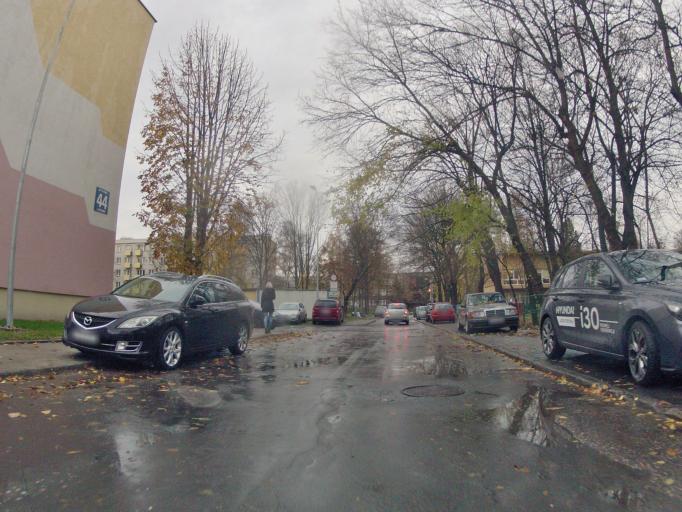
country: PL
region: Lesser Poland Voivodeship
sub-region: Powiat wielicki
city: Czarnochowice
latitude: 50.0745
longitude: 20.0223
